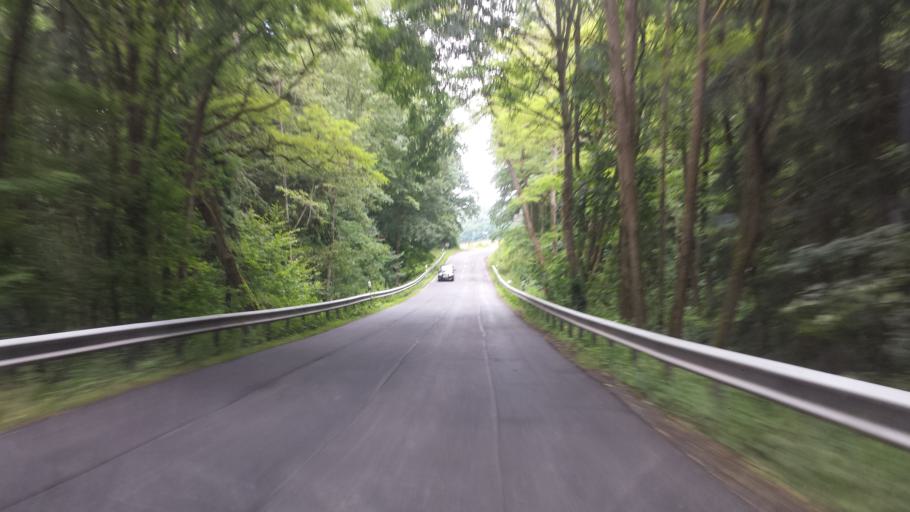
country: DE
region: Rheinland-Pfalz
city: Ramsen
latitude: 49.5353
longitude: 8.0313
